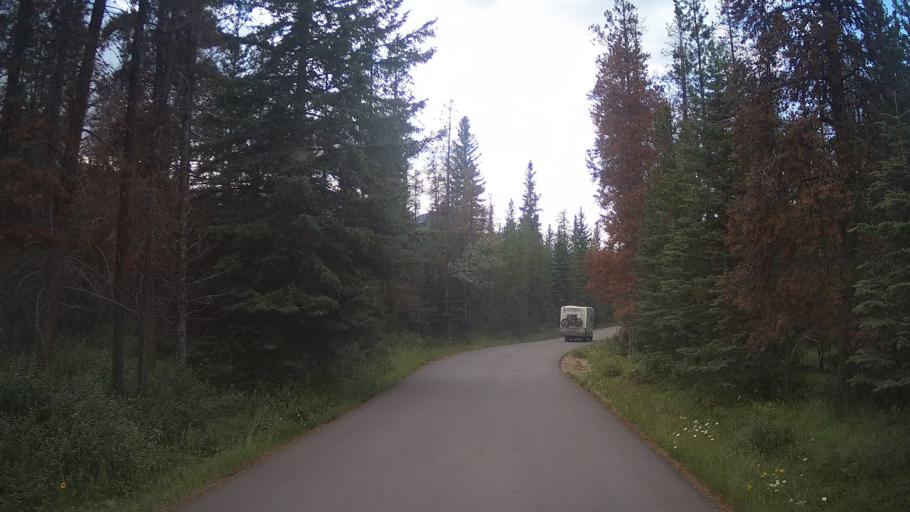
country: CA
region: Alberta
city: Jasper Park Lodge
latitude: 52.9295
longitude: -118.0307
